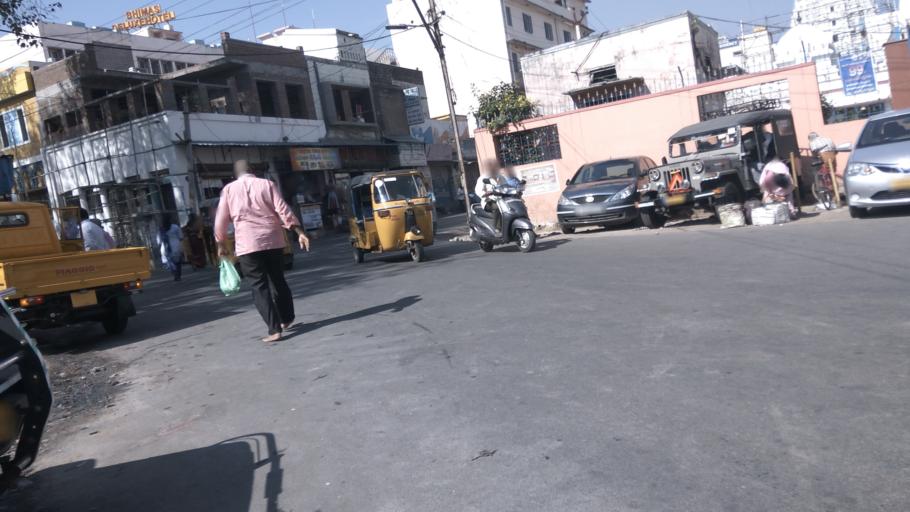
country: IN
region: Andhra Pradesh
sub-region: Chittoor
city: Tirupati
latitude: 13.6299
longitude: 79.4202
